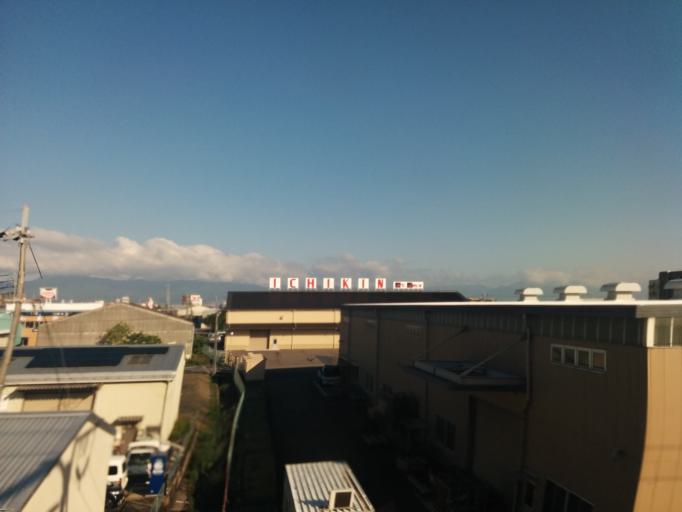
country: JP
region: Shiga Prefecture
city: Kusatsu
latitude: 35.0200
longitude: 135.9803
